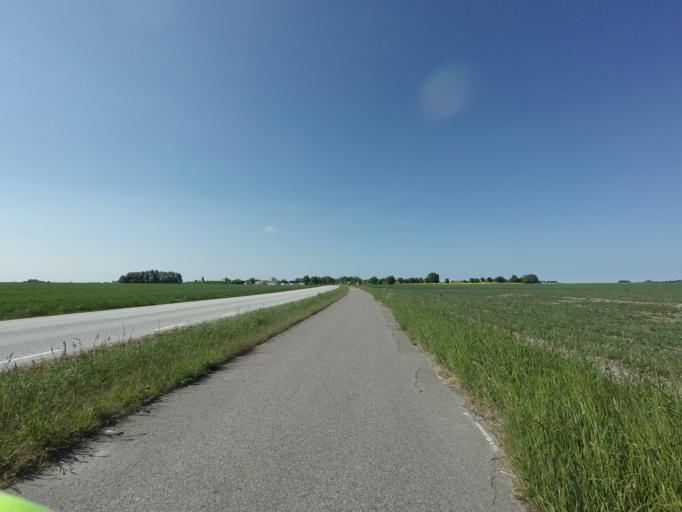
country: SE
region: Skane
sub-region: Vellinge Kommun
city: Vellinge
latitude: 55.4652
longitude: 13.0040
